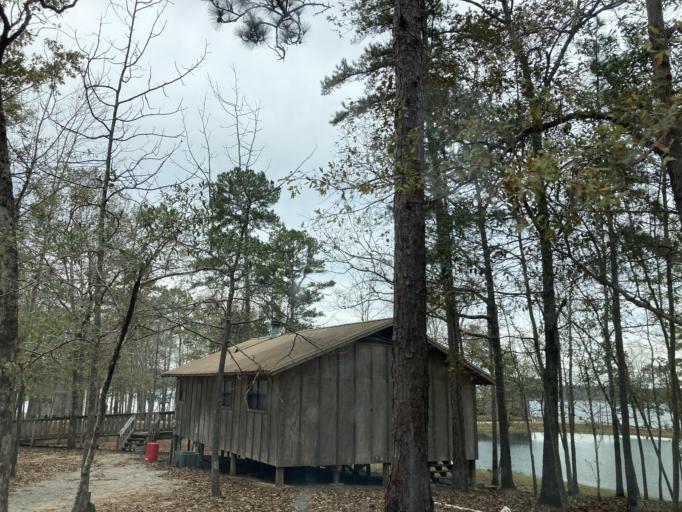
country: US
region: Mississippi
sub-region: Lamar County
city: Lumberton
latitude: 31.0823
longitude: -89.4985
